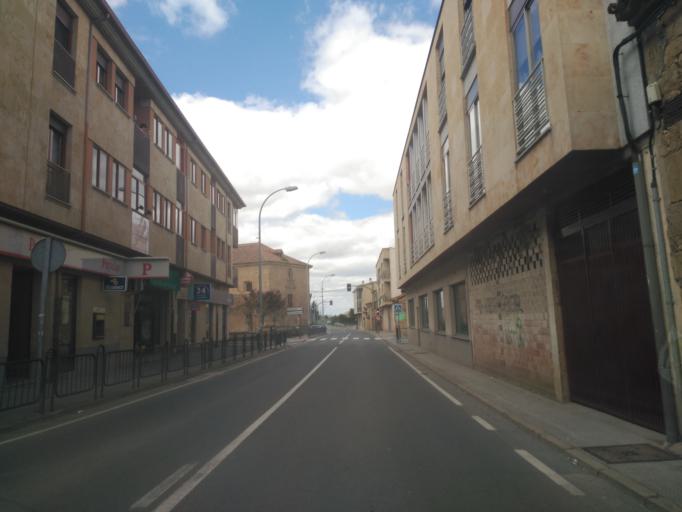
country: ES
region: Castille and Leon
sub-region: Provincia de Salamanca
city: Villamayor
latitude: 40.9991
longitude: -5.6961
